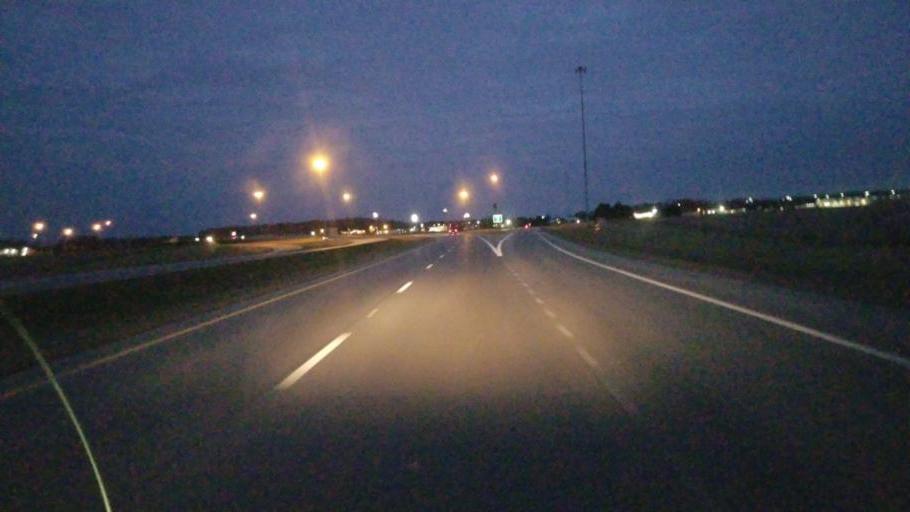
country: US
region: Ohio
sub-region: Wyandot County
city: Upper Sandusky
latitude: 40.8277
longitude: -83.2369
